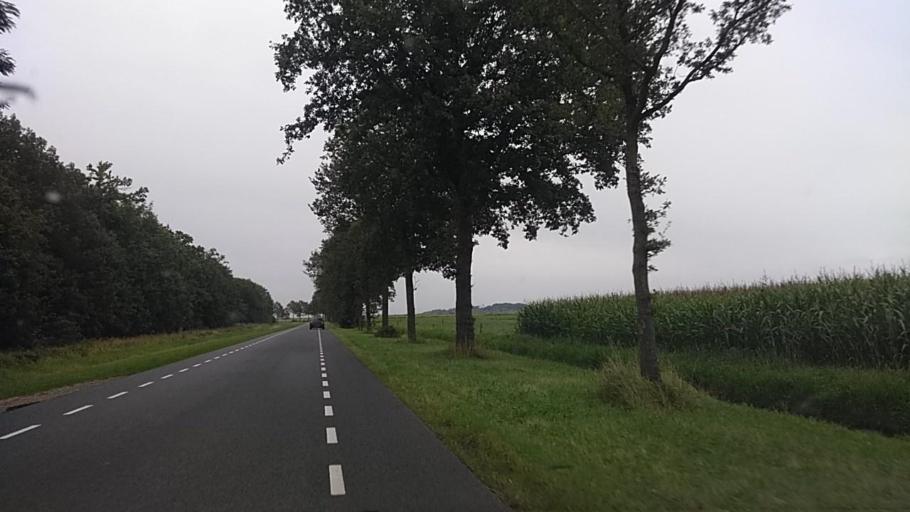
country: NL
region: Overijssel
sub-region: Gemeente Steenwijkerland
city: Vollenhove
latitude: 52.6570
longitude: 5.9710
